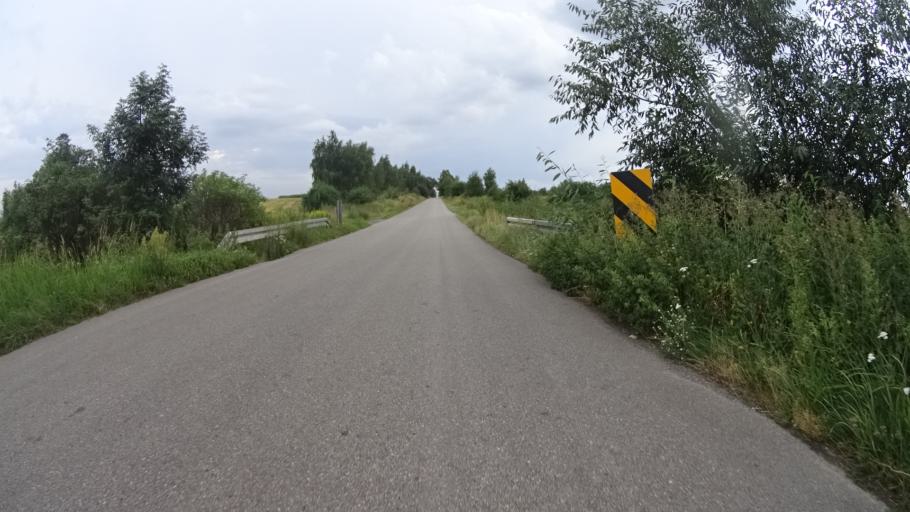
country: PL
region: Masovian Voivodeship
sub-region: Powiat grojecki
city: Goszczyn
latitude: 51.6717
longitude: 20.8574
